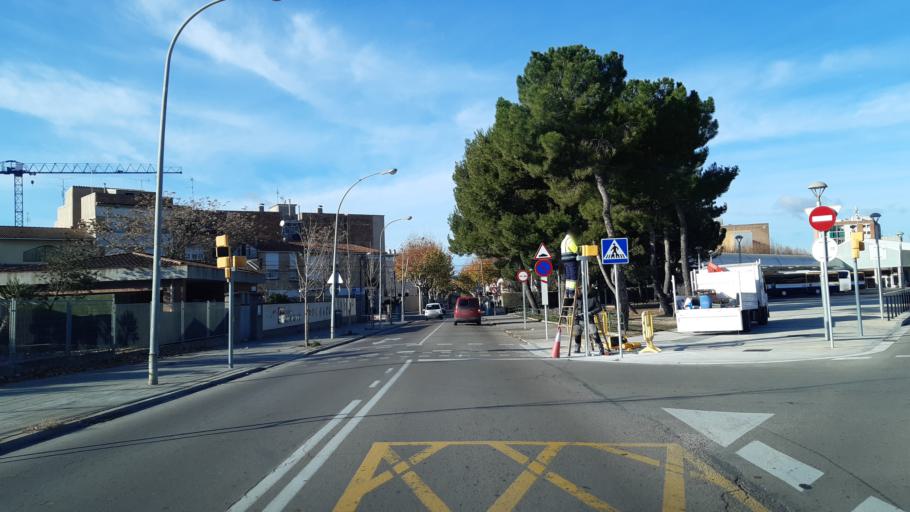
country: ES
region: Catalonia
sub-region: Provincia de Barcelona
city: Vilanova del Cami
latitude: 41.5772
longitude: 1.6328
